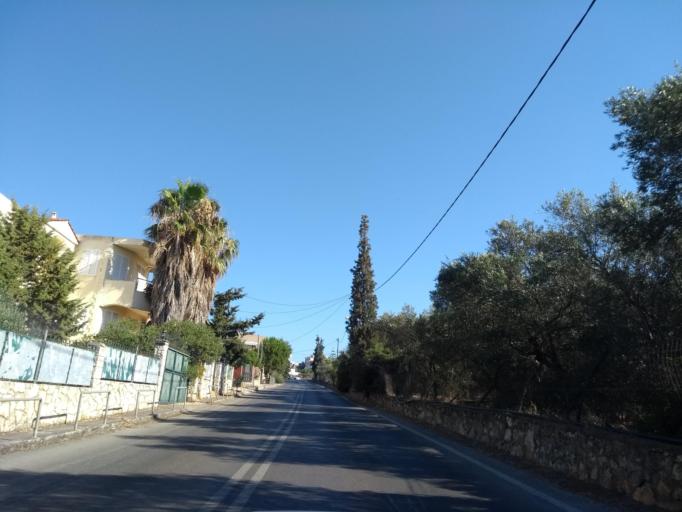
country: GR
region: Crete
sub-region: Nomos Chanias
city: Pithari
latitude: 35.5372
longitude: 24.0813
